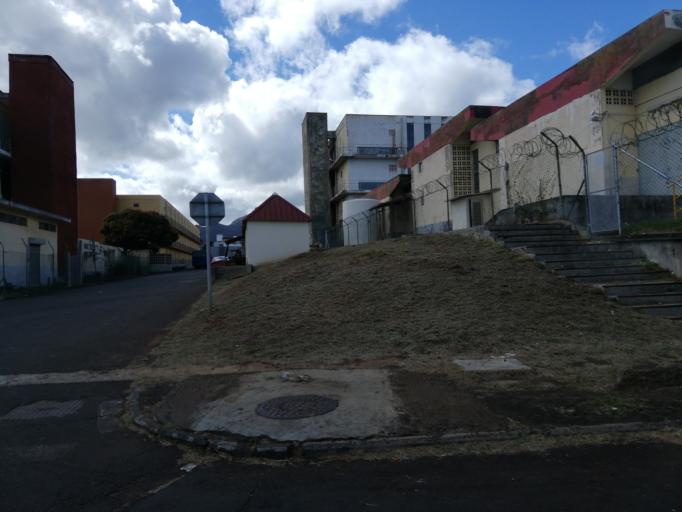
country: MU
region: Moka
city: Pailles
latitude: -20.1873
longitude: 57.4671
